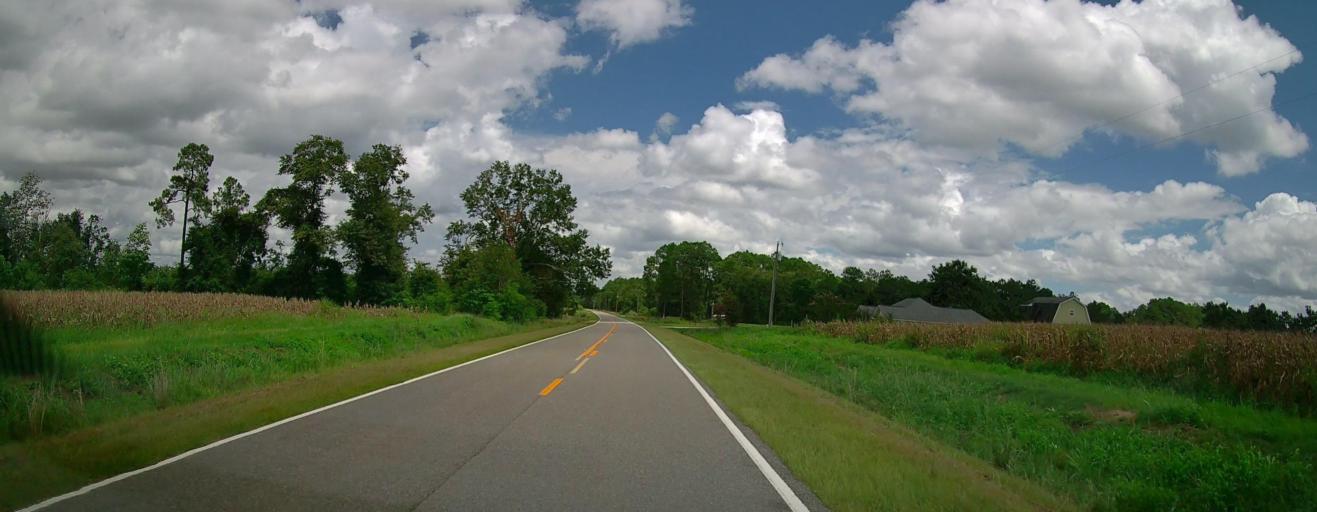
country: US
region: Georgia
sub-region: Irwin County
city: Ocilla
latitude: 31.6458
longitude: -83.3278
